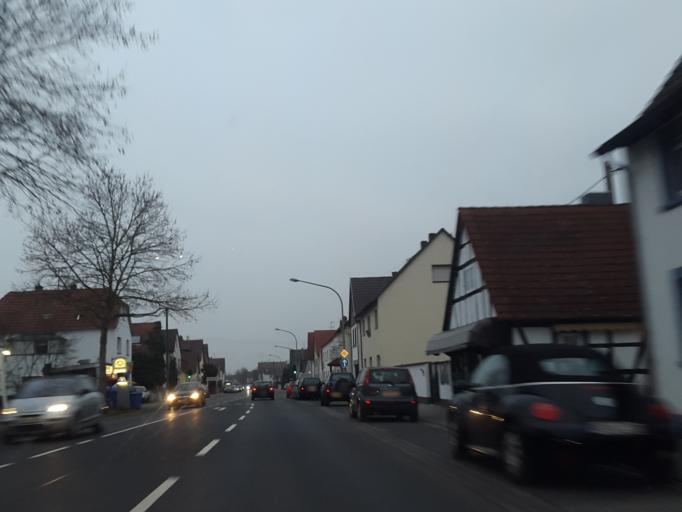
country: DE
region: Bavaria
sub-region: Regierungsbezirk Unterfranken
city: Kahl am Main
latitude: 50.0400
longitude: 9.0335
